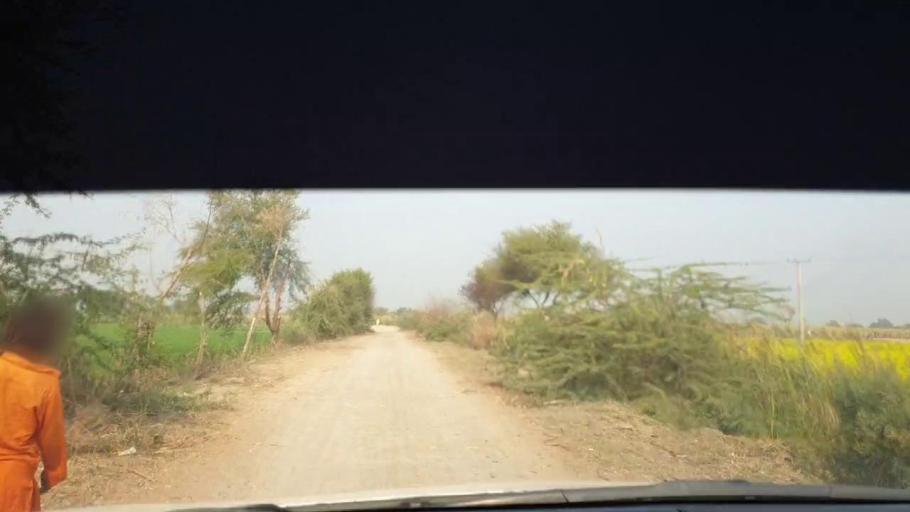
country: PK
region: Sindh
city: Berani
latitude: 25.8061
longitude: 68.8363
